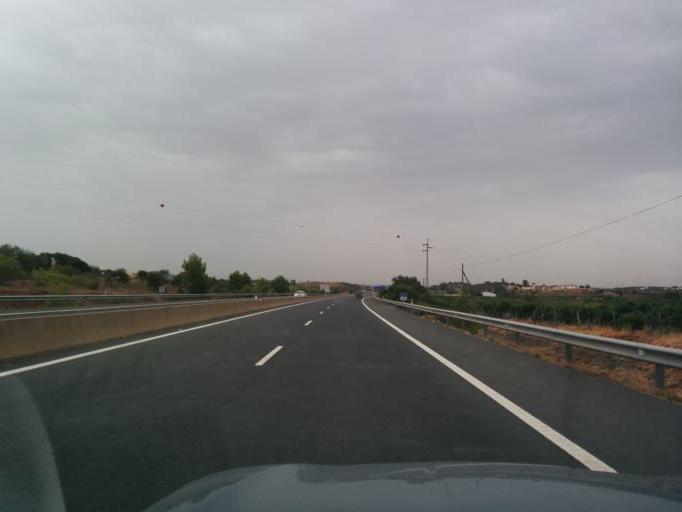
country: PT
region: Faro
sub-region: Vila Real de Santo Antonio
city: Monte Gordo
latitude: 37.1997
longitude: -7.5184
